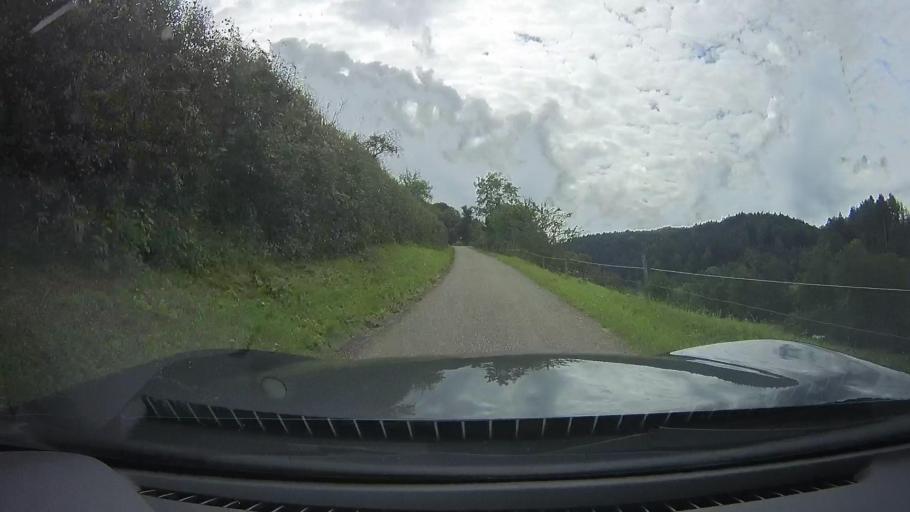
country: DE
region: Baden-Wuerttemberg
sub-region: Regierungsbezirk Stuttgart
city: Kaisersbach
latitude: 48.9592
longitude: 9.6418
